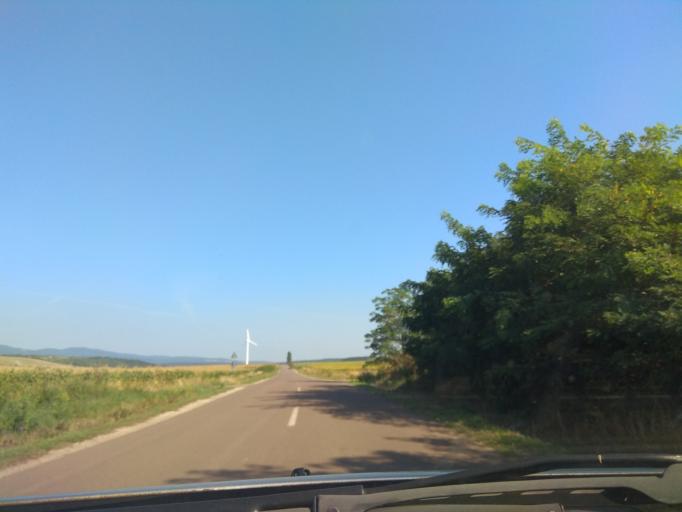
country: HU
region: Borsod-Abauj-Zemplen
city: Emod
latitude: 47.9614
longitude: 20.8037
